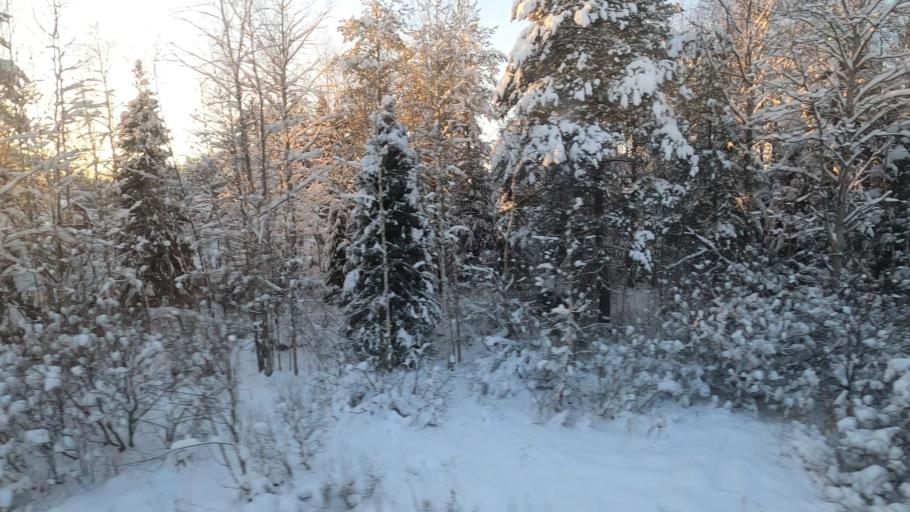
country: RU
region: Moskovskaya
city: Verbilki
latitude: 56.5334
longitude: 37.5600
